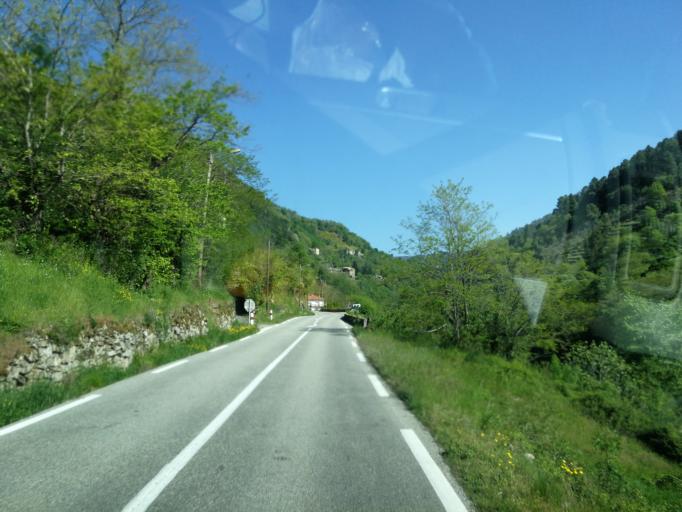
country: FR
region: Rhone-Alpes
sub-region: Departement de l'Ardeche
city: Saint-Sauveur-de-Montagut
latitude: 44.8265
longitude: 4.5770
